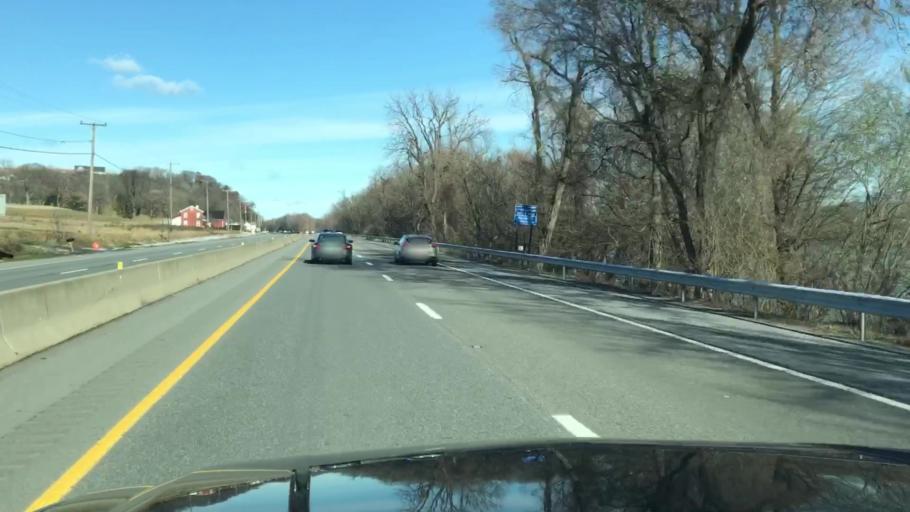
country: US
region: Pennsylvania
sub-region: Snyder County
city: Selinsgrove
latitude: 40.7341
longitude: -76.8558
